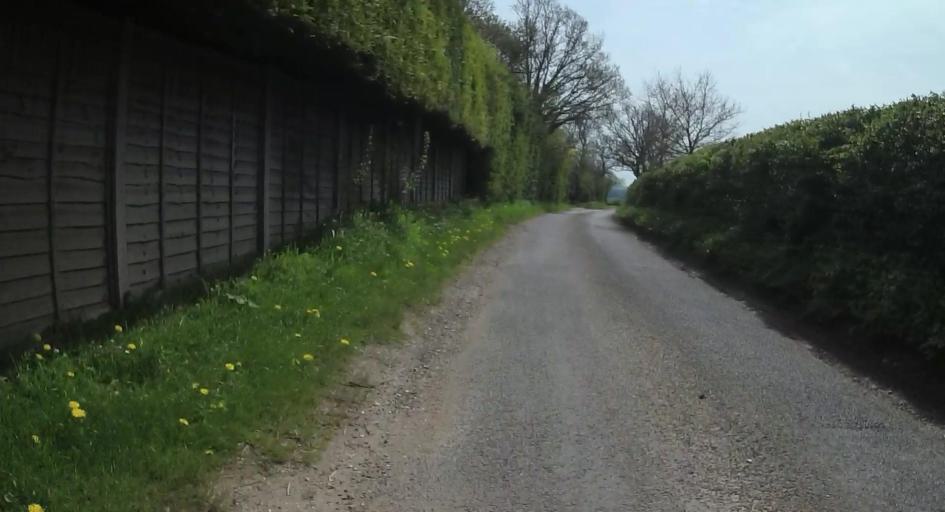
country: GB
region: England
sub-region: Hampshire
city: Alton
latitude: 51.1784
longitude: -0.9661
